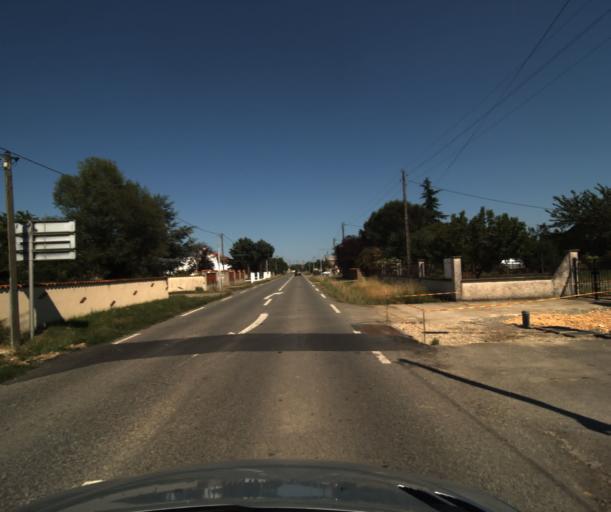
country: FR
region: Midi-Pyrenees
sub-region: Departement de la Haute-Garonne
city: Labarthe-sur-Leze
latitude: 43.4592
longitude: 1.3756
